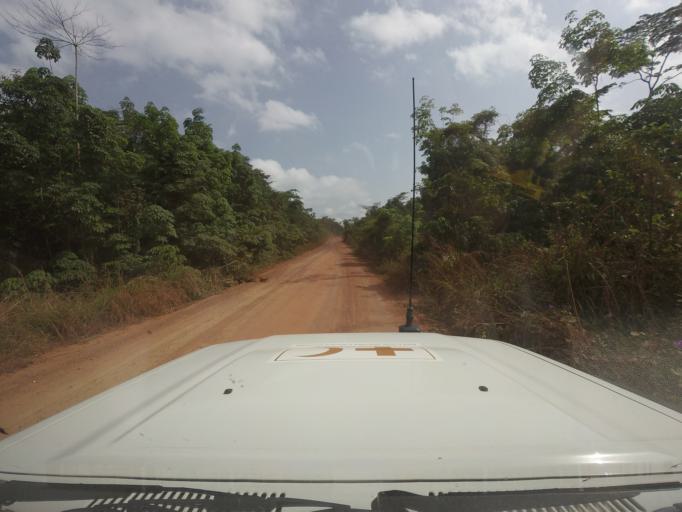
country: LR
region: Bong
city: Gbarnga
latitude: 7.2080
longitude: -9.4417
